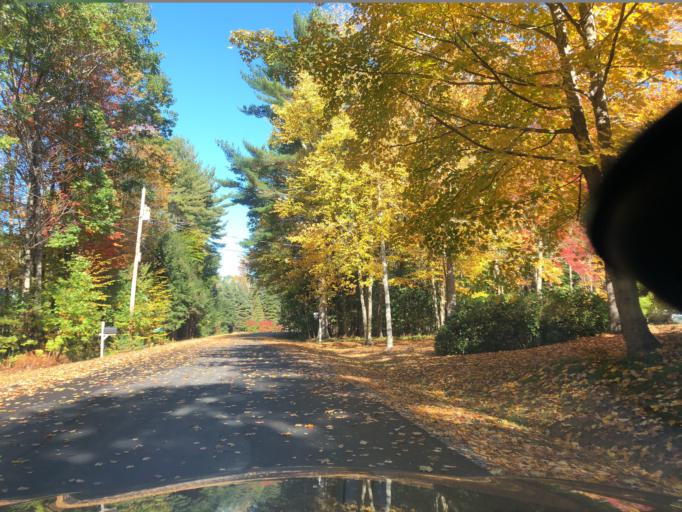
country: US
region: New Hampshire
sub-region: Strafford County
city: Lee
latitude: 43.1206
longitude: -71.0023
